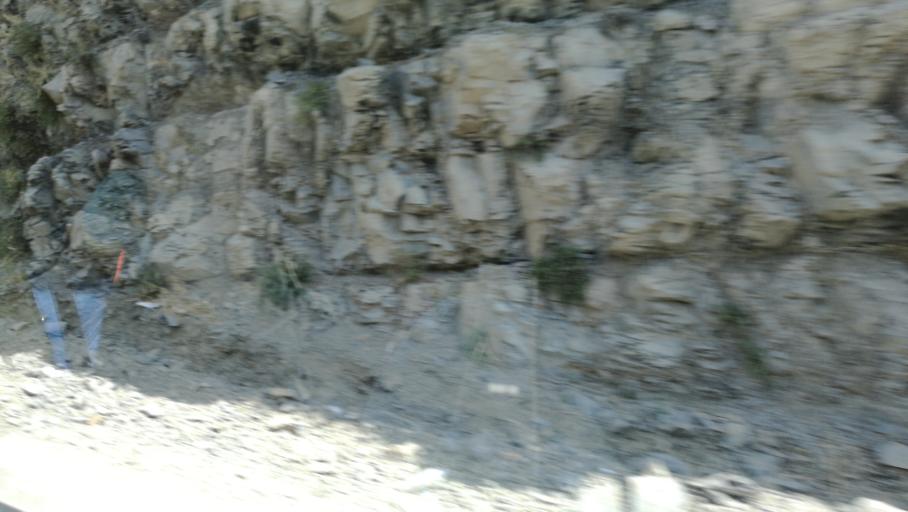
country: IR
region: Alborz
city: Karaj
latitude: 35.9397
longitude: 51.0742
